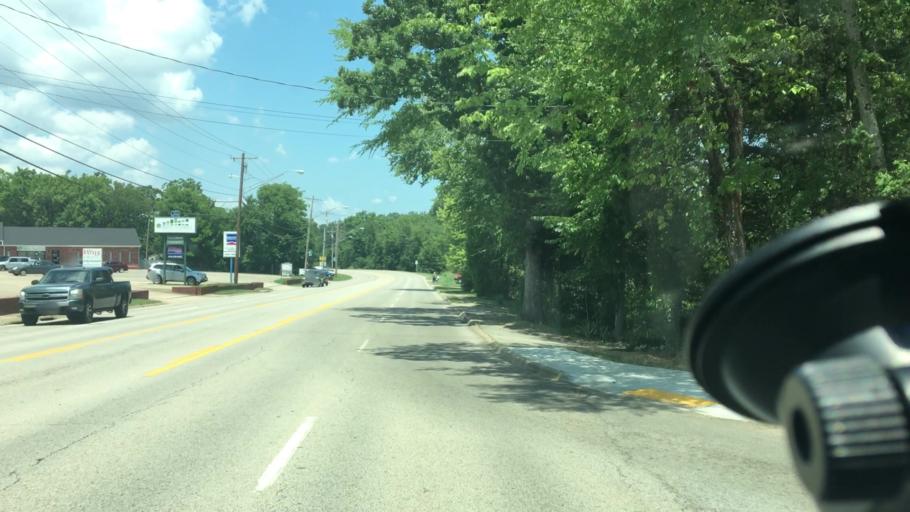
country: US
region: Arkansas
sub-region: Sebastian County
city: Barling
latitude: 35.3328
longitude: -94.3103
